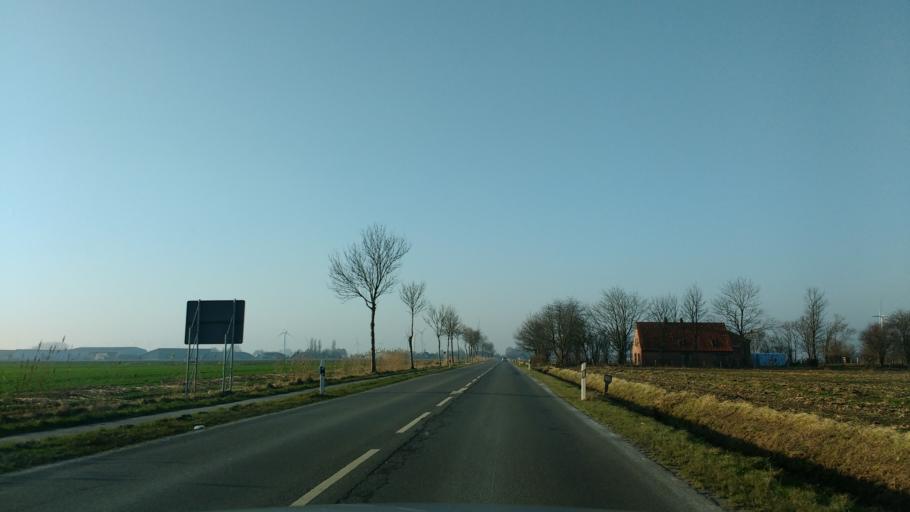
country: DE
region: Schleswig-Holstein
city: Kronprinzenkoog
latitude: 53.9871
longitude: 8.9775
